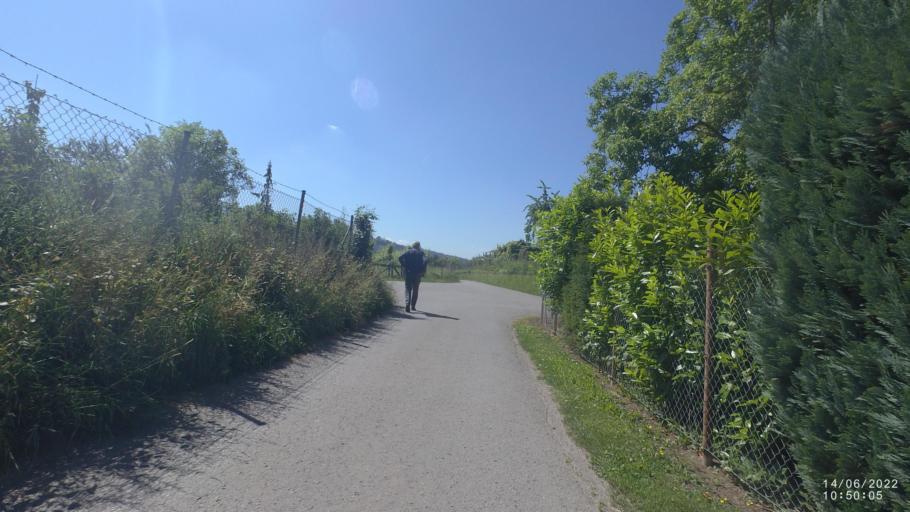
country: DE
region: Baden-Wuerttemberg
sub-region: Regierungsbezirk Stuttgart
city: Fellbach
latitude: 48.8010
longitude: 9.2582
